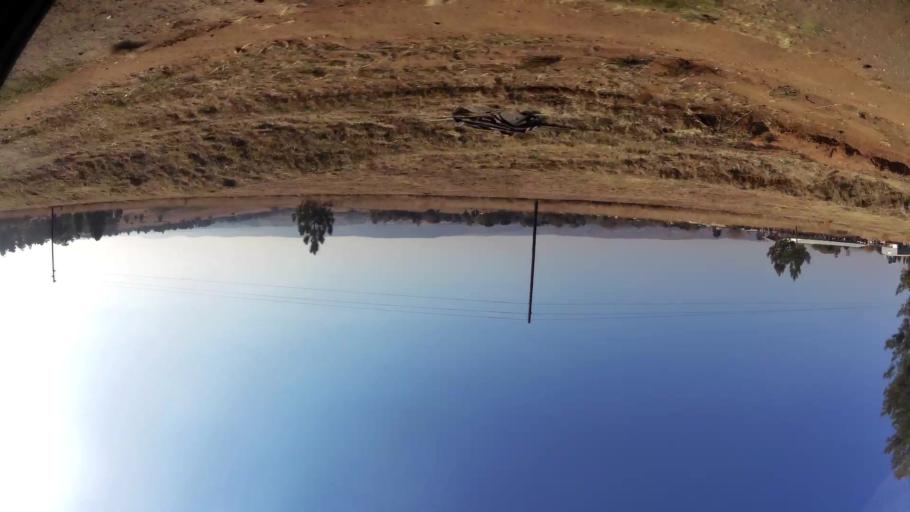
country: ZA
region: Gauteng
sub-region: West Rand District Municipality
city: Muldersdriseloop
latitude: -26.0478
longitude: 27.8897
